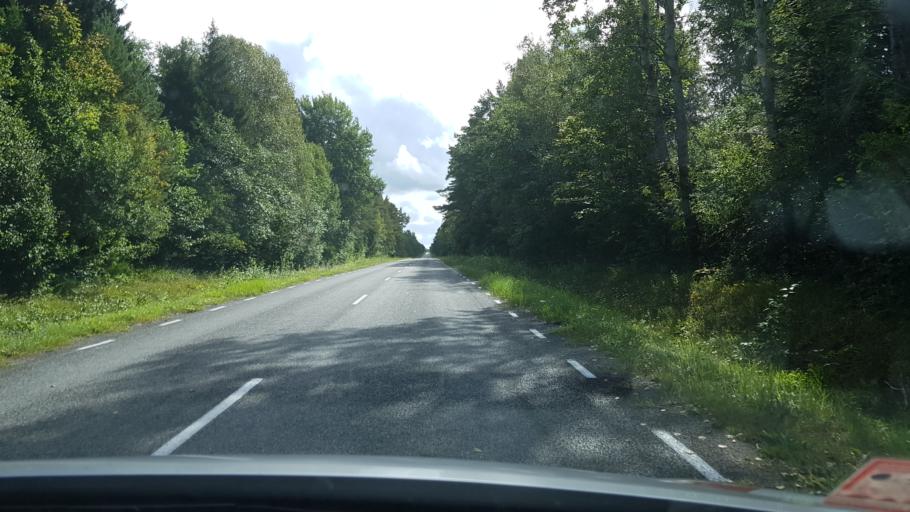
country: EE
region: Saare
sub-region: Kuressaare linn
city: Kuressaare
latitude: 58.3786
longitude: 22.0344
